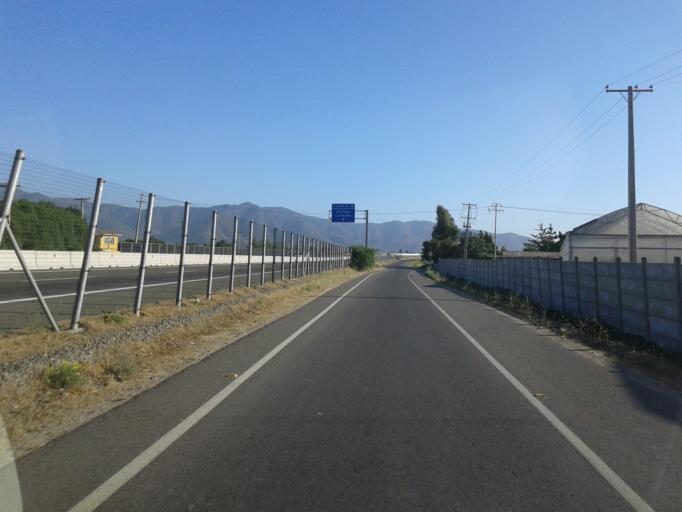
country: CL
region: Valparaiso
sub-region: Provincia de Quillota
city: Quillota
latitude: -32.8547
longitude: -71.2246
